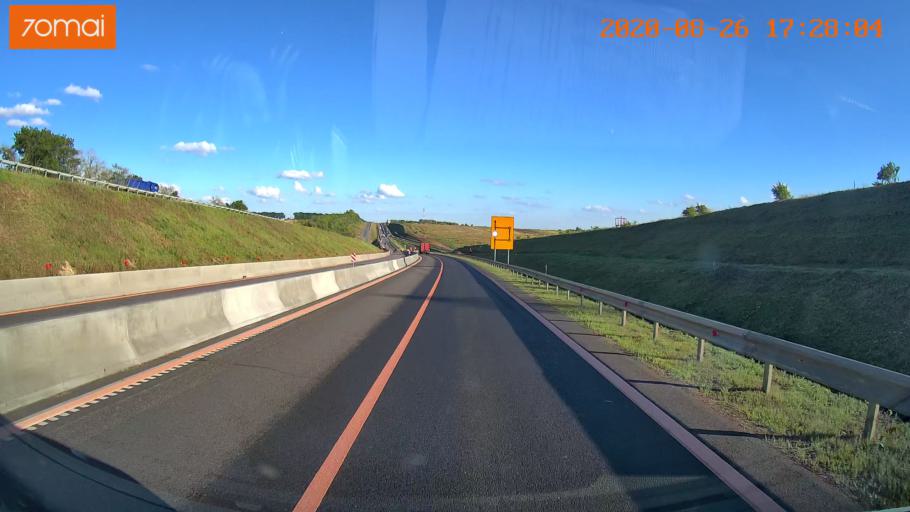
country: RU
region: Tula
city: Kazachka
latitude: 53.4663
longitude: 38.1292
